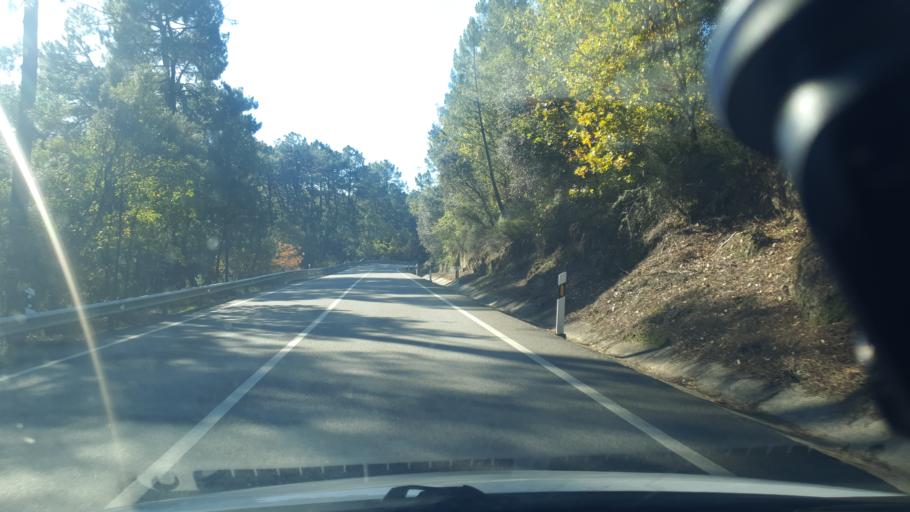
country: ES
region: Castille and Leon
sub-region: Provincia de Avila
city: Mombeltran
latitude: 40.2180
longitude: -5.0376
